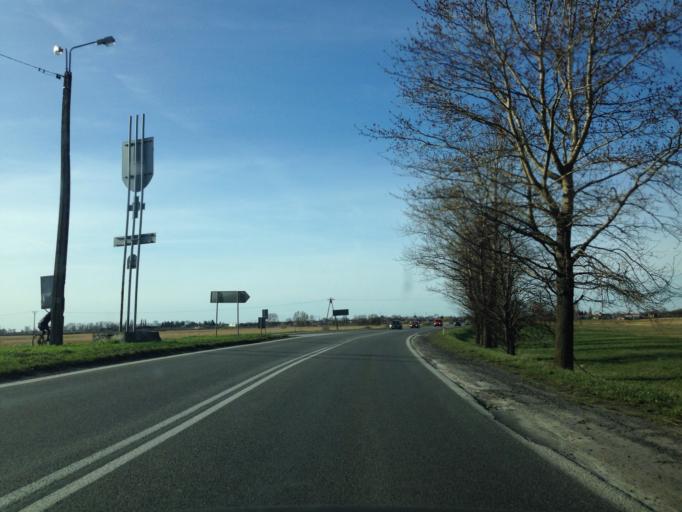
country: PL
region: Lodz Voivodeship
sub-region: Powiat leczycki
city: Leczyca
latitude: 52.0662
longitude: 19.1971
